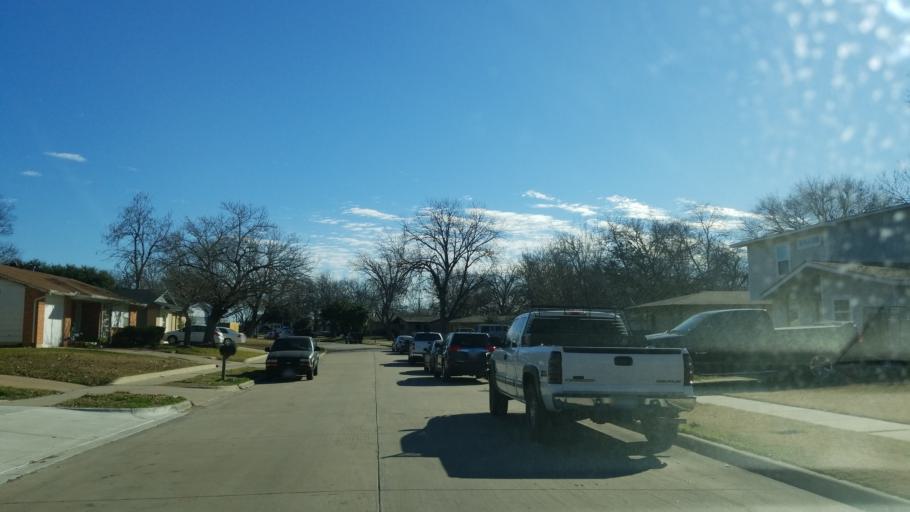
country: US
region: Texas
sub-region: Tarrant County
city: Arlington
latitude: 32.7287
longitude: -97.0595
